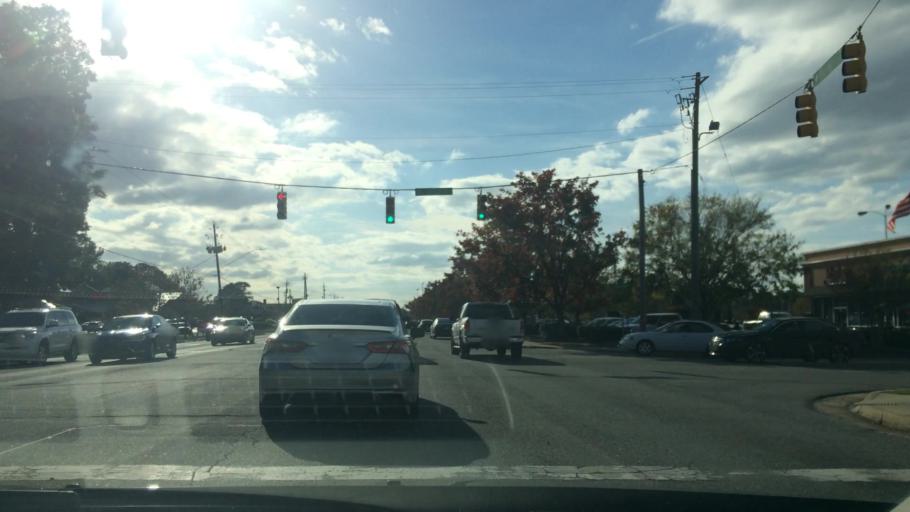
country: US
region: North Carolina
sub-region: Wayne County
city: Elroy
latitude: 35.3763
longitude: -77.9410
